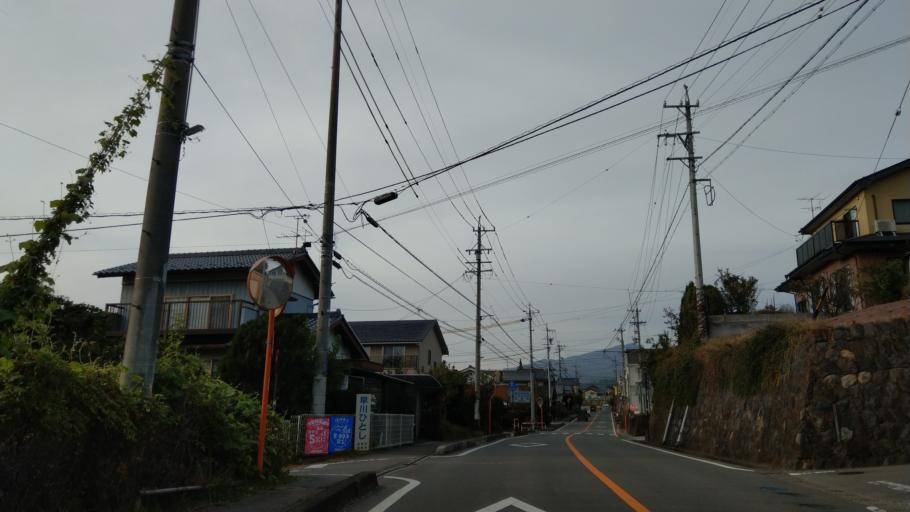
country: JP
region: Nagano
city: Komoro
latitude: 36.3197
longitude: 138.4279
